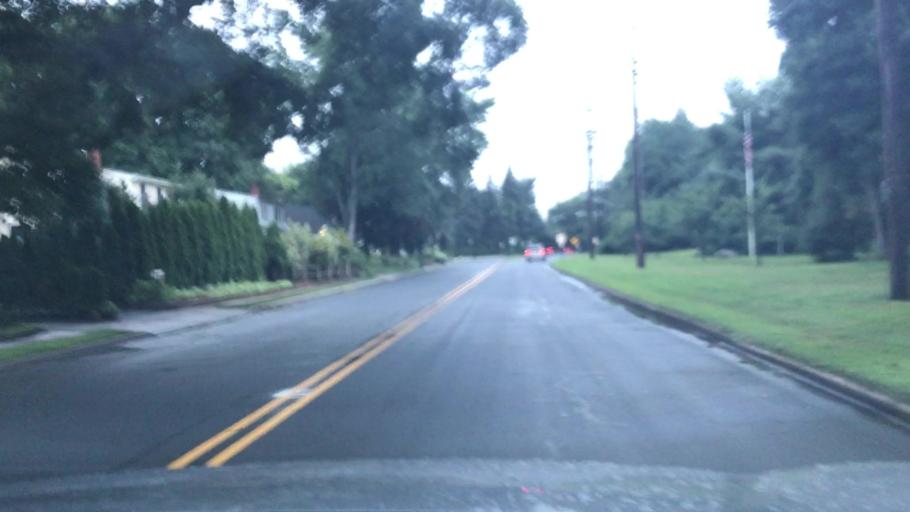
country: US
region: New Jersey
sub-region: Bergen County
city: Tenafly
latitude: 40.9154
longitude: -73.9666
